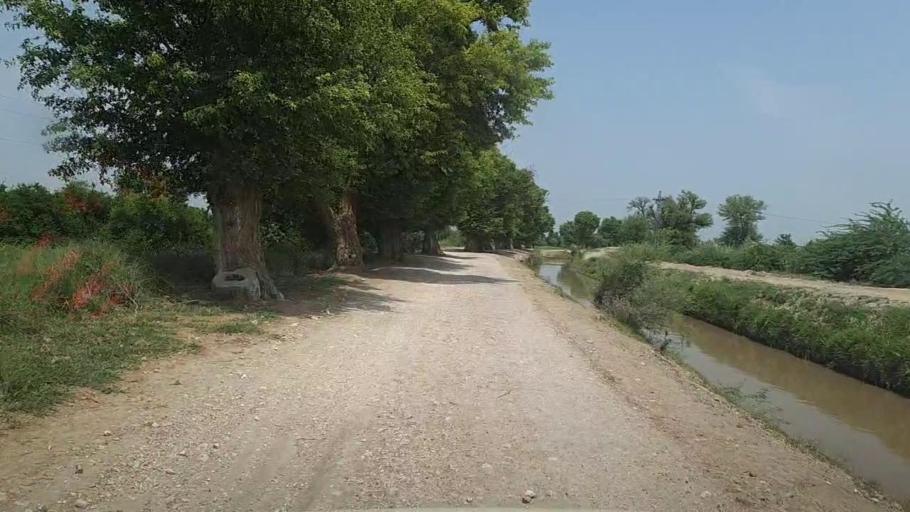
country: PK
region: Sindh
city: Karaundi
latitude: 26.9032
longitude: 68.3308
